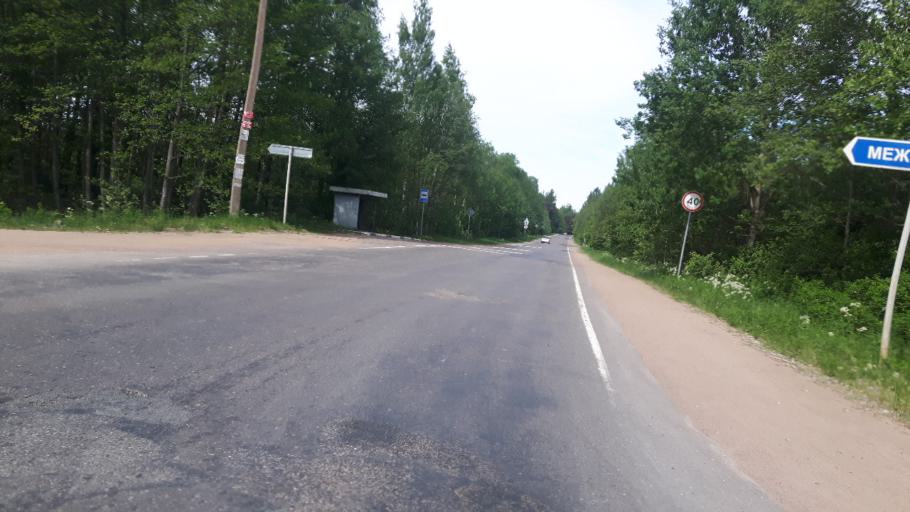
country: RU
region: Leningrad
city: Ust'-Luga
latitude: 59.6457
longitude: 28.2681
